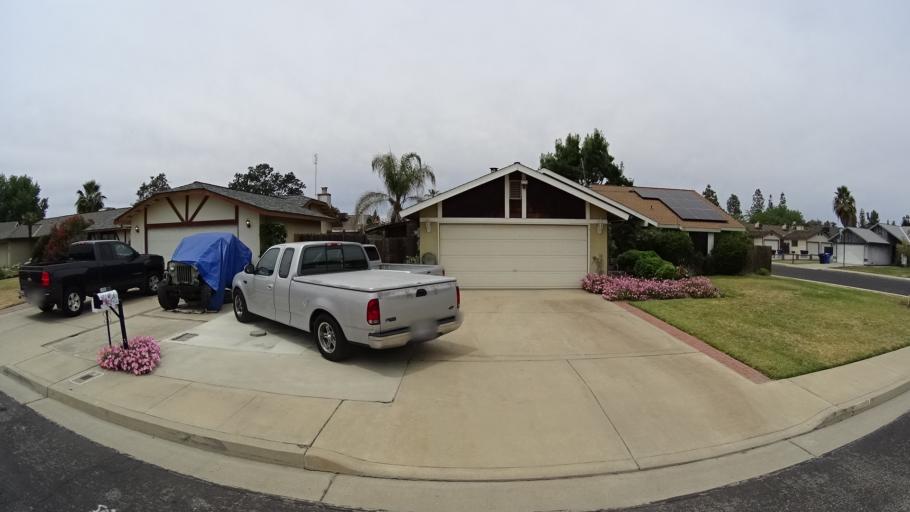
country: US
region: California
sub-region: Kings County
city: Hanford
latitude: 36.3517
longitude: -119.6359
